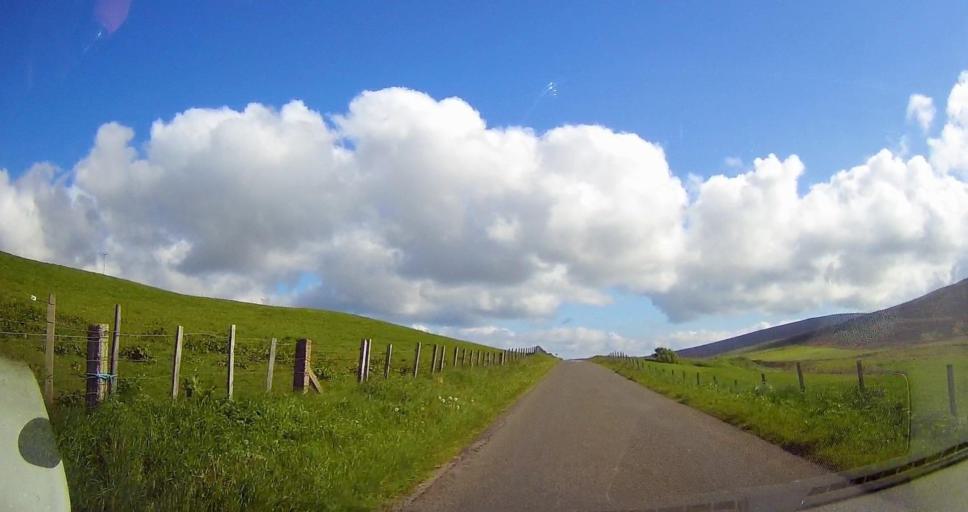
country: GB
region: Scotland
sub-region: Orkney Islands
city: Stromness
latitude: 58.9784
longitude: -3.1354
